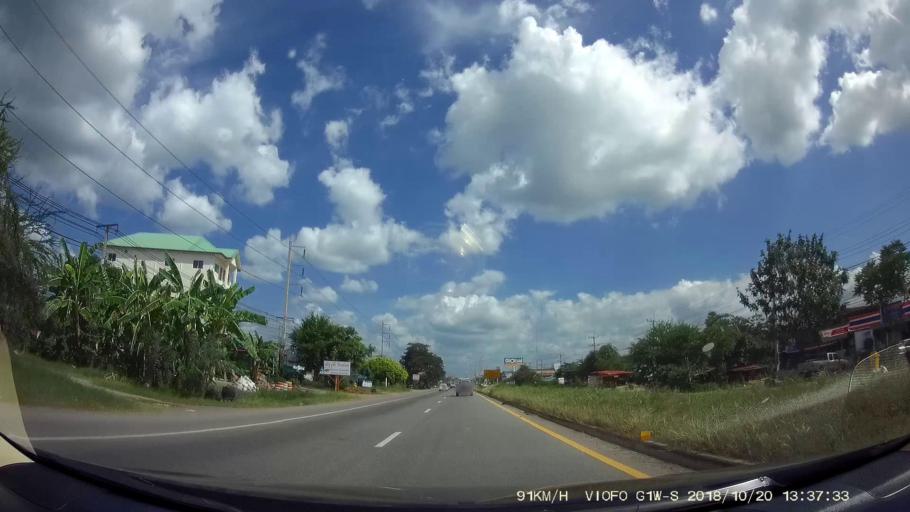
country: TH
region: Khon Kaen
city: Chum Phae
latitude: 16.5573
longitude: 102.0723
